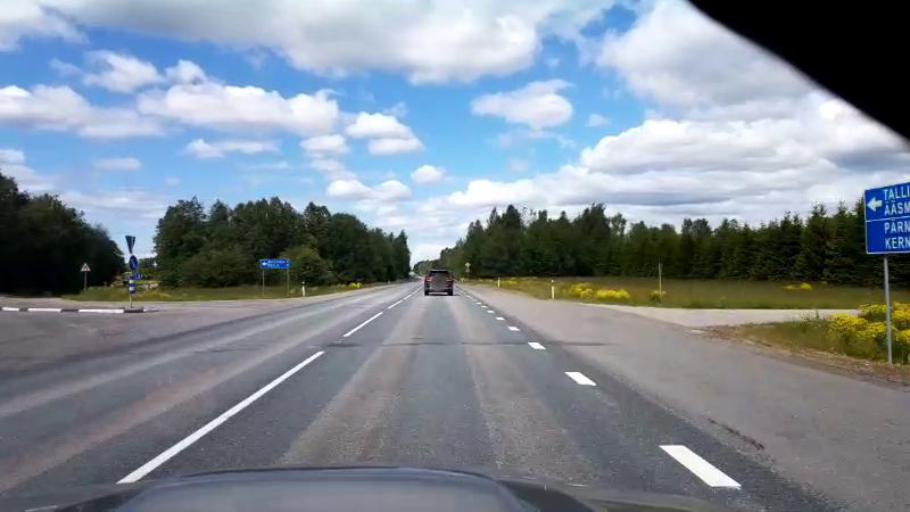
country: EE
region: Harju
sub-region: Saue linn
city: Saue
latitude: 59.1617
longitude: 24.5046
